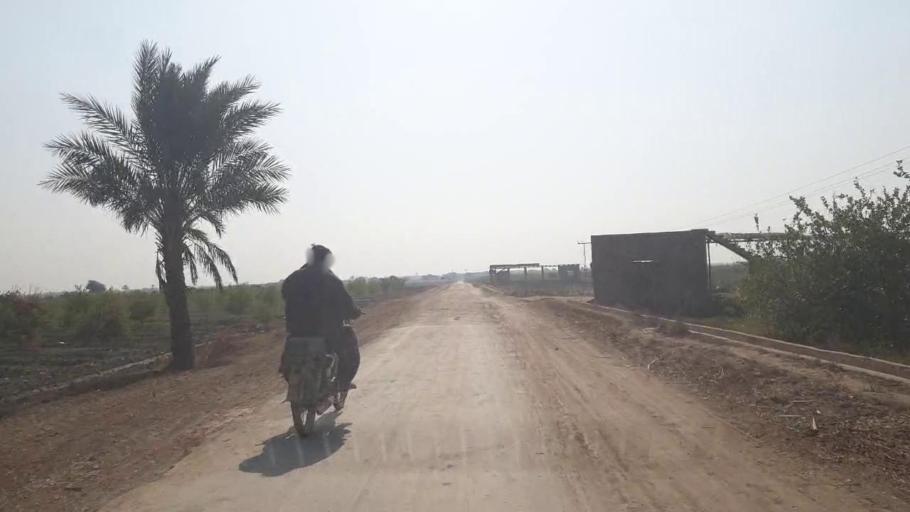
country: PK
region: Sindh
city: Tando Allahyar
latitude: 25.4631
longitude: 68.8138
